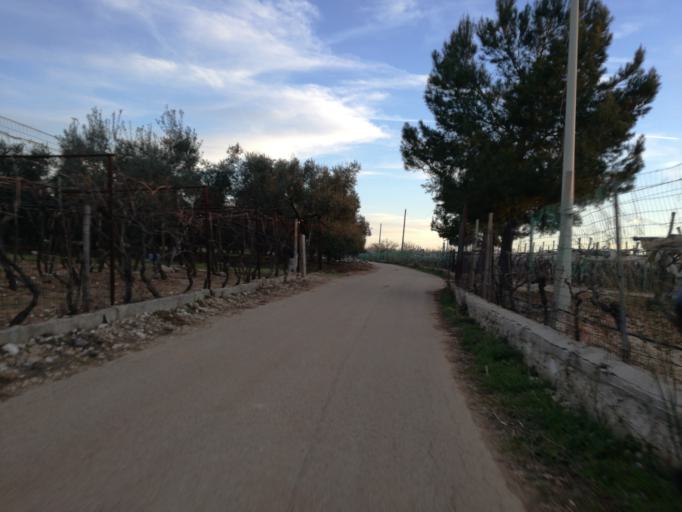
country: IT
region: Apulia
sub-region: Provincia di Bari
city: Adelfia
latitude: 41.0150
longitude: 16.8718
